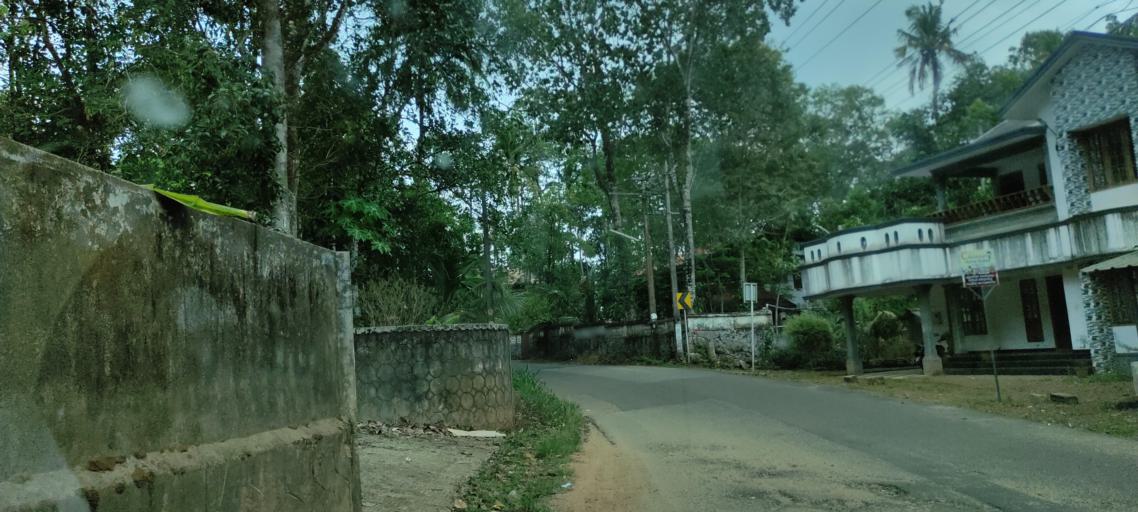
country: IN
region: Kerala
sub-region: Pattanamtitta
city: Adur
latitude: 9.1715
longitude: 76.7370
